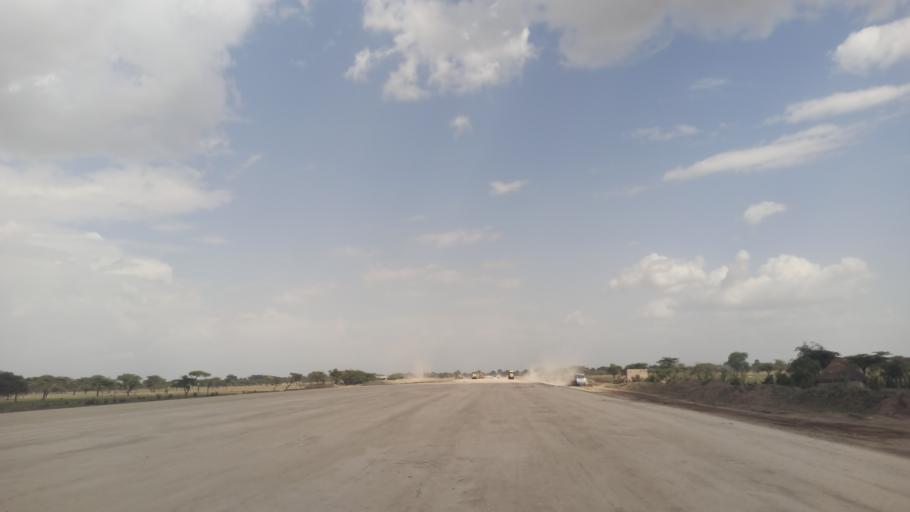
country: ET
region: Oromiya
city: Ziway
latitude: 7.7233
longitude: 38.6294
